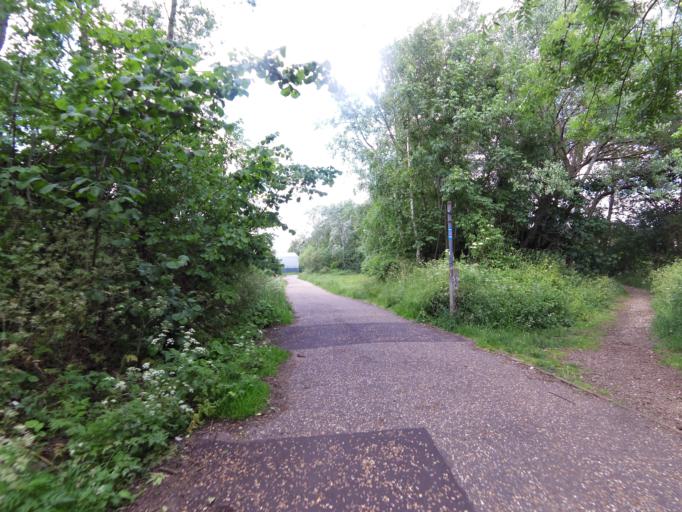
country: GB
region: England
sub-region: Norfolk
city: Norwich
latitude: 52.6365
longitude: 1.2871
